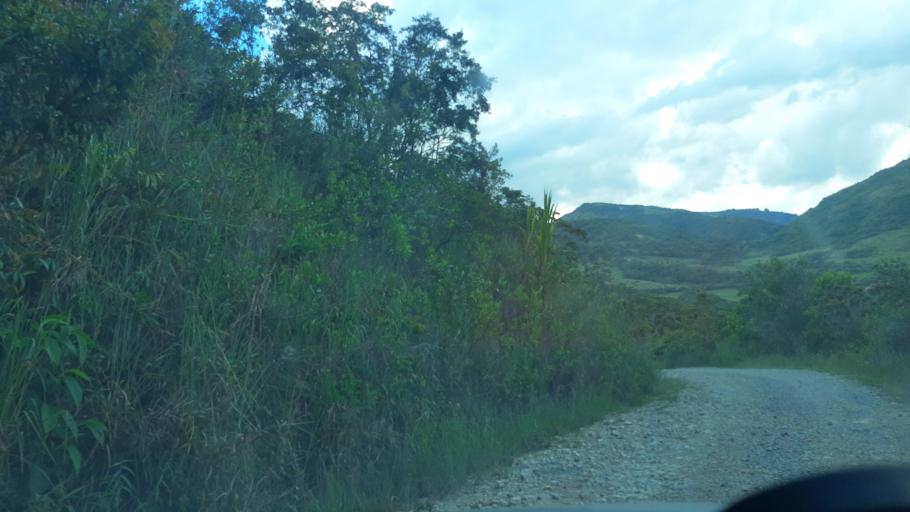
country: CO
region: Boyaca
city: Santa Sofia
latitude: 5.7472
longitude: -73.5772
